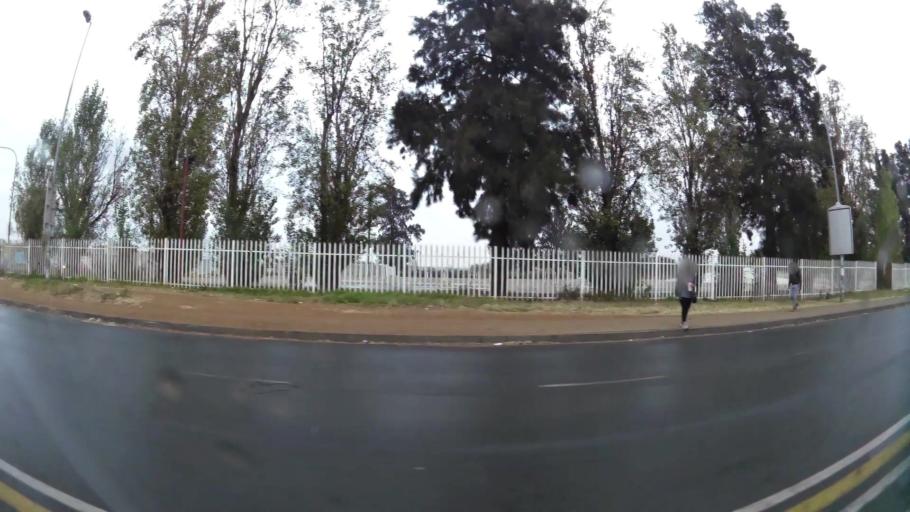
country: ZA
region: Gauteng
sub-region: City of Johannesburg Metropolitan Municipality
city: Soweto
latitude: -26.2647
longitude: 27.8578
